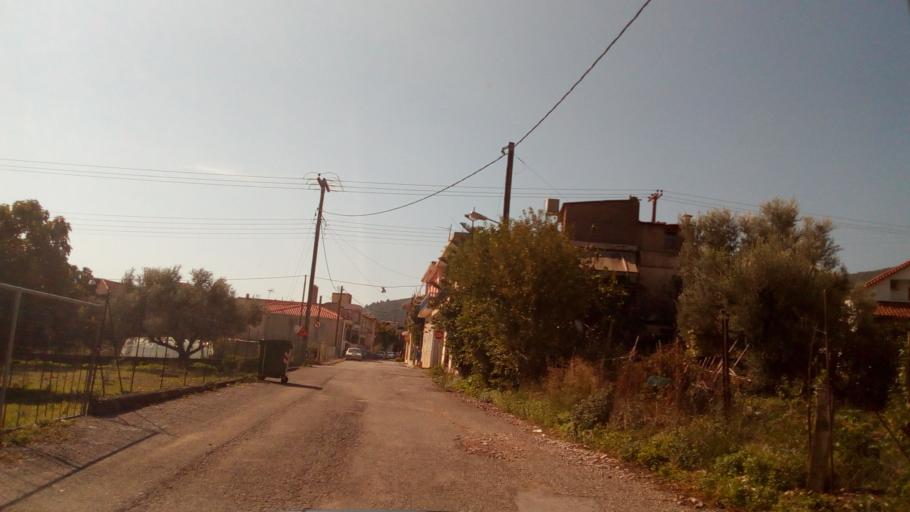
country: GR
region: West Greece
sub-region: Nomos Aitolias kai Akarnanias
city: Nafpaktos
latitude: 38.4086
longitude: 21.8510
